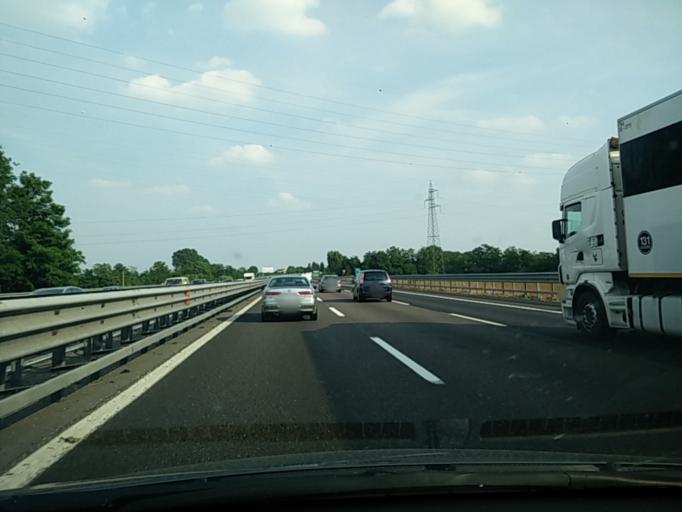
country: IT
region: Lombardy
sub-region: Citta metropolitana di Milano
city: Figino
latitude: 45.4778
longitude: 9.0761
